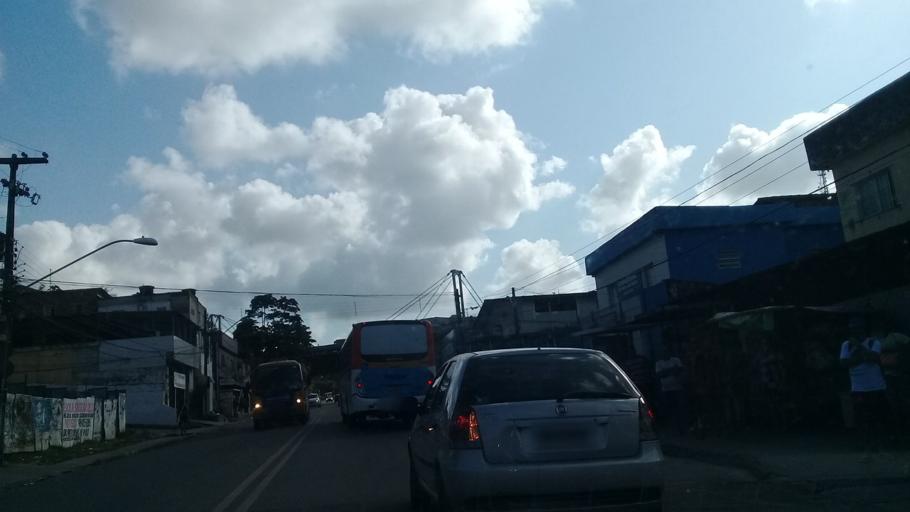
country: BR
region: Pernambuco
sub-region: Jaboatao Dos Guararapes
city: Jaboatao dos Guararapes
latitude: -8.1181
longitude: -34.9422
